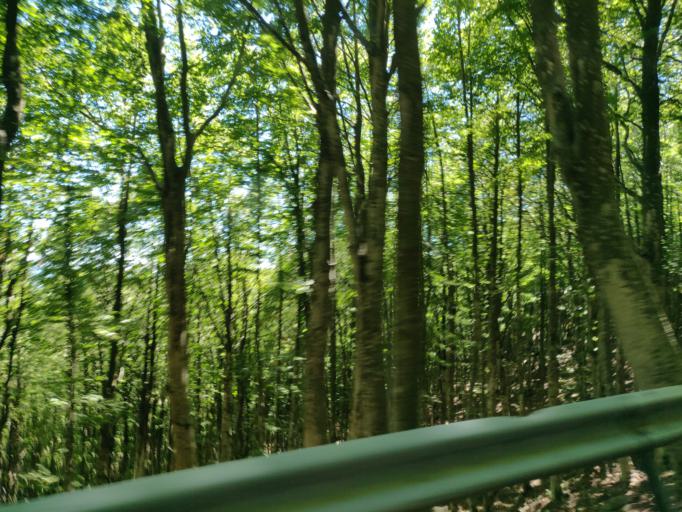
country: IT
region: Tuscany
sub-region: Provincia di Siena
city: Abbadia San Salvatore
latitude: 42.8869
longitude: 11.6279
